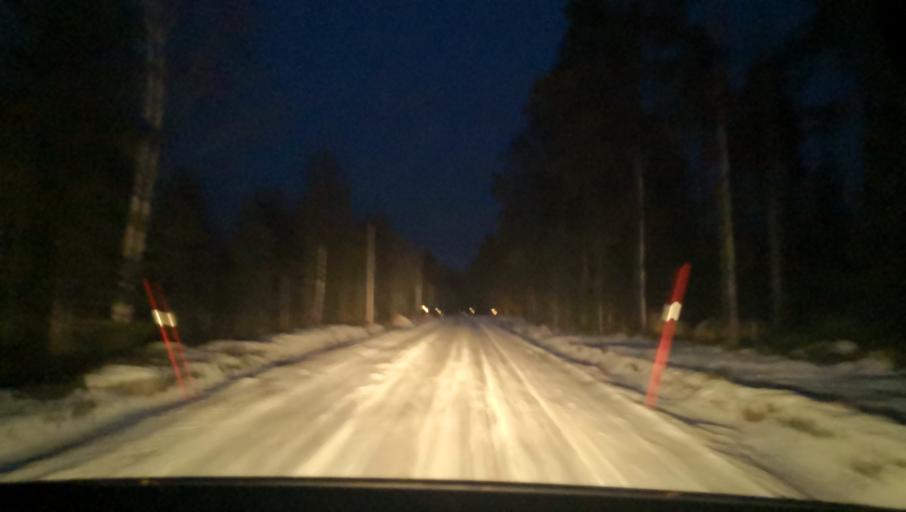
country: SE
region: Uppsala
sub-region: Heby Kommun
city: Tarnsjo
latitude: 60.2694
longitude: 16.7936
